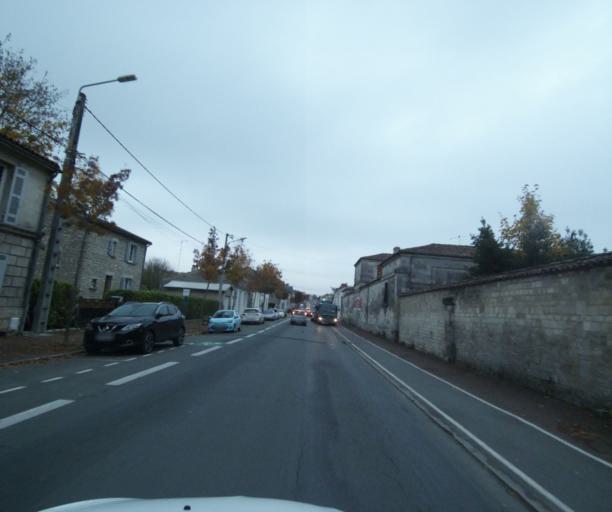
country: FR
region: Poitou-Charentes
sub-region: Departement de la Charente-Maritime
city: Saintes
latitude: 45.7452
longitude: -0.6153
